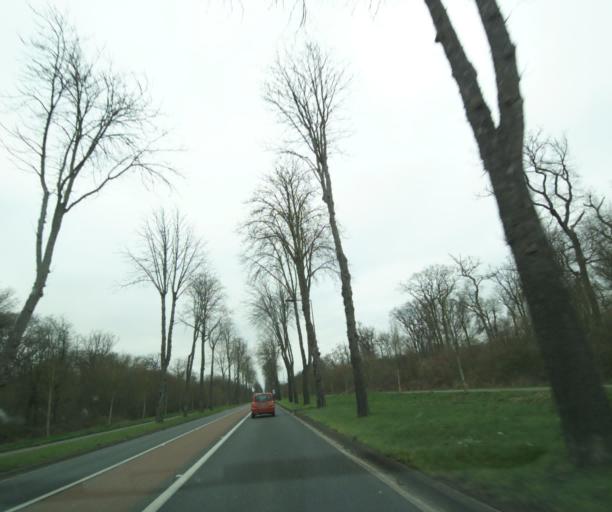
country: FR
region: Ile-de-France
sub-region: Departement des Yvelines
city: Saint-Germain-en-Laye
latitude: 48.9129
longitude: 2.0703
